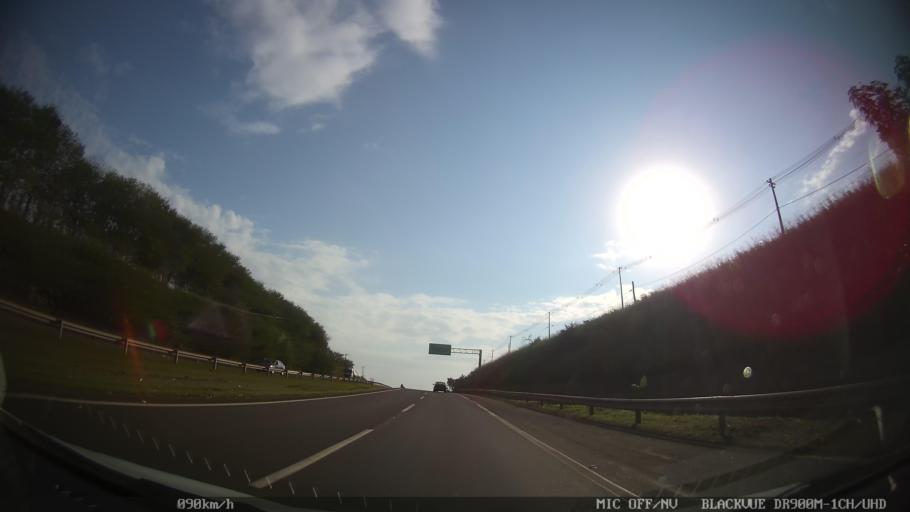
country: BR
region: Sao Paulo
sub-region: Cosmopolis
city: Cosmopolis
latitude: -22.6562
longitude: -47.1780
